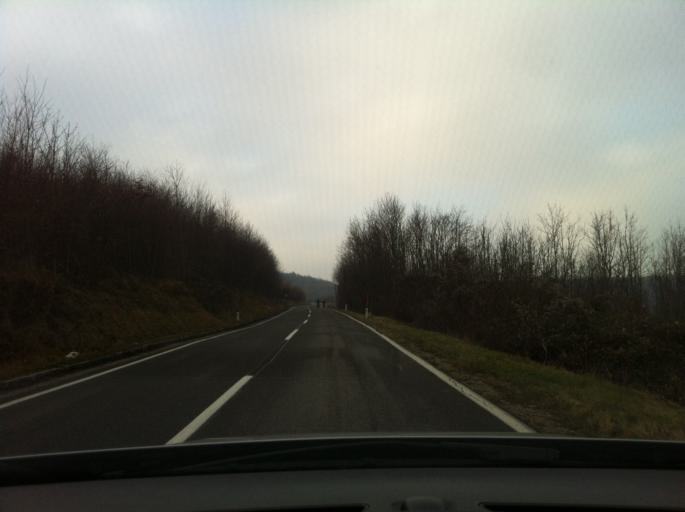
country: AT
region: Lower Austria
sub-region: Politischer Bezirk Wien-Umgebung
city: Mauerbach
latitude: 48.2474
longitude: 16.2552
